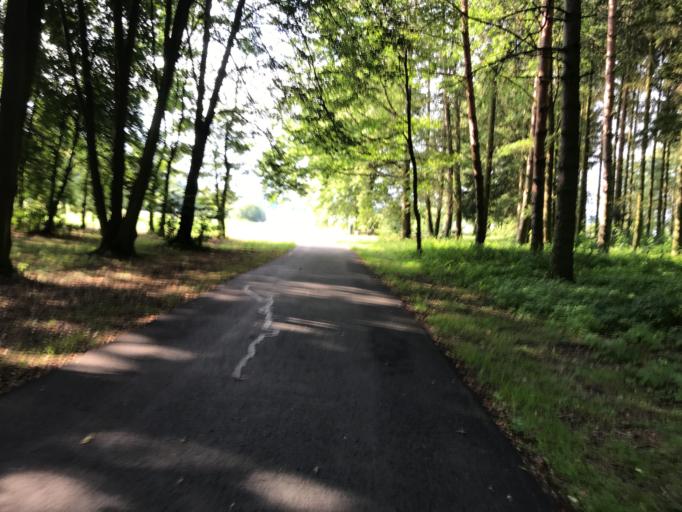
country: CZ
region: Jihocesky
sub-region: Okres Jindrichuv Hradec
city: Trebon
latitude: 48.9991
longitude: 14.7471
